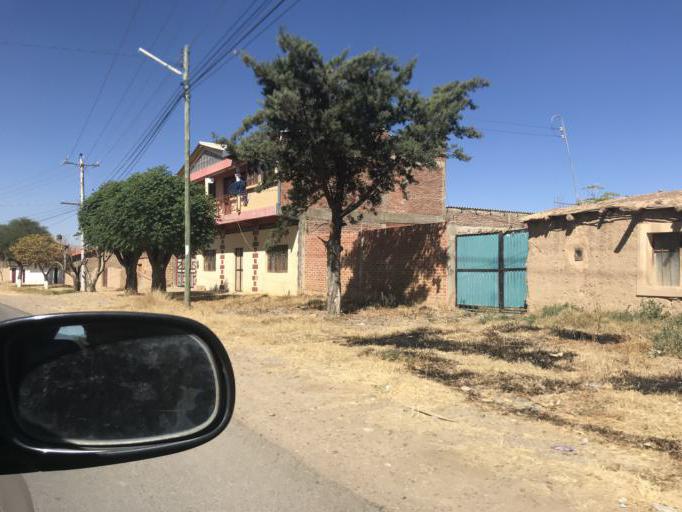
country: BO
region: Cochabamba
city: Tarata
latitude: -17.6025
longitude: -65.9788
